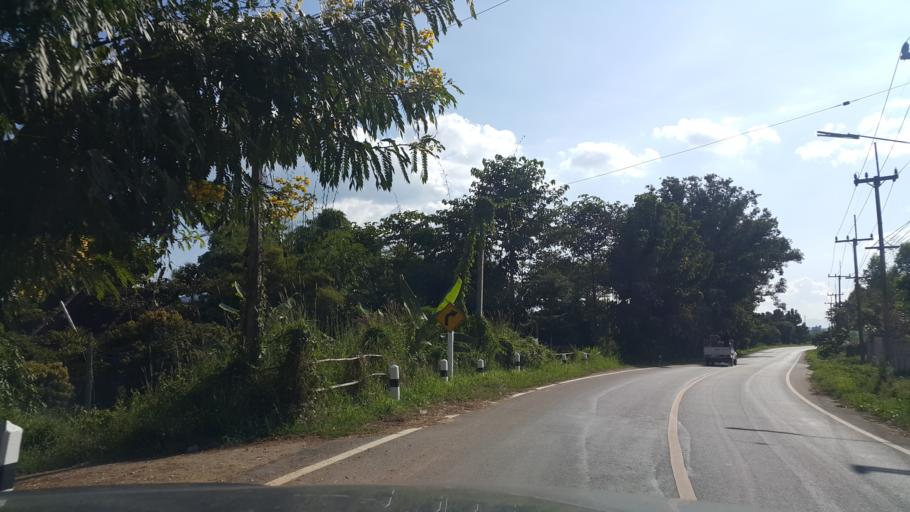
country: TH
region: Lamphun
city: Mae Tha
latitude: 18.5592
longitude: 99.2568
